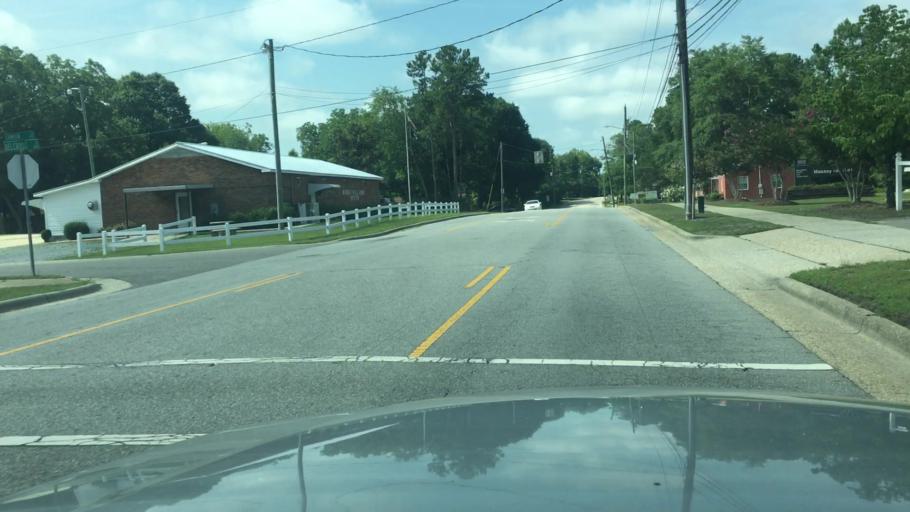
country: US
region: North Carolina
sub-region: Cumberland County
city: Fayetteville
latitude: 35.0291
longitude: -78.8974
